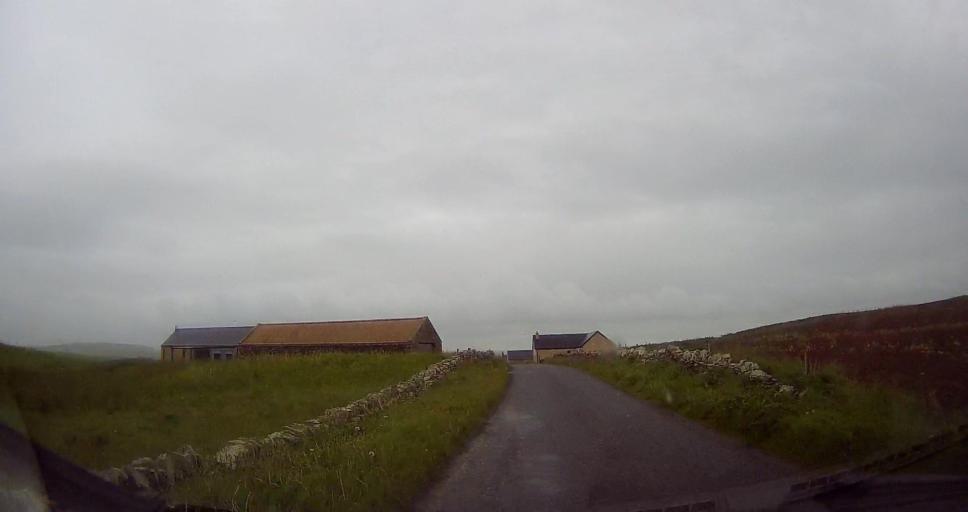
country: GB
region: Scotland
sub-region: Orkney Islands
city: Stromness
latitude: 59.0694
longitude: -3.3077
